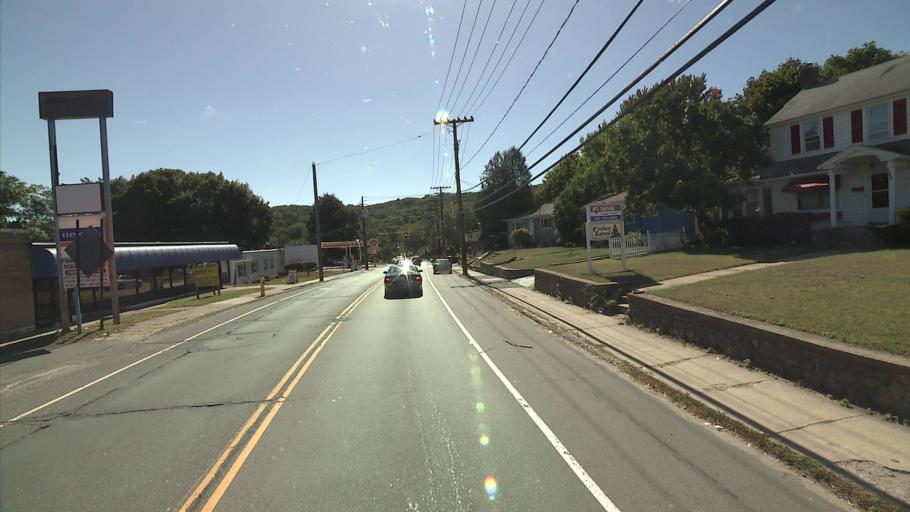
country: US
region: Connecticut
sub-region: New Haven County
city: Waterbury
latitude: 41.5394
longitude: -73.0204
